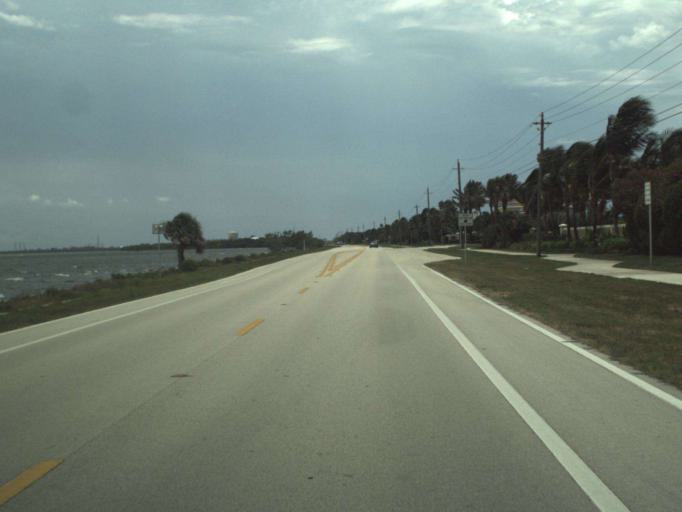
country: US
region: Florida
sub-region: Saint Lucie County
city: Hutchinson Island South
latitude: 27.3142
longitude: -80.2243
